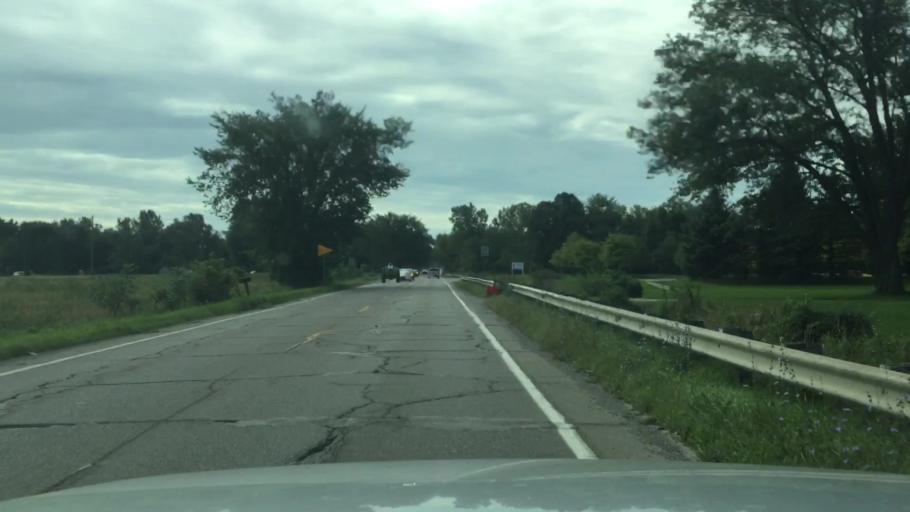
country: US
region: Michigan
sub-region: Wayne County
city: Belleville
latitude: 42.1816
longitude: -83.4832
